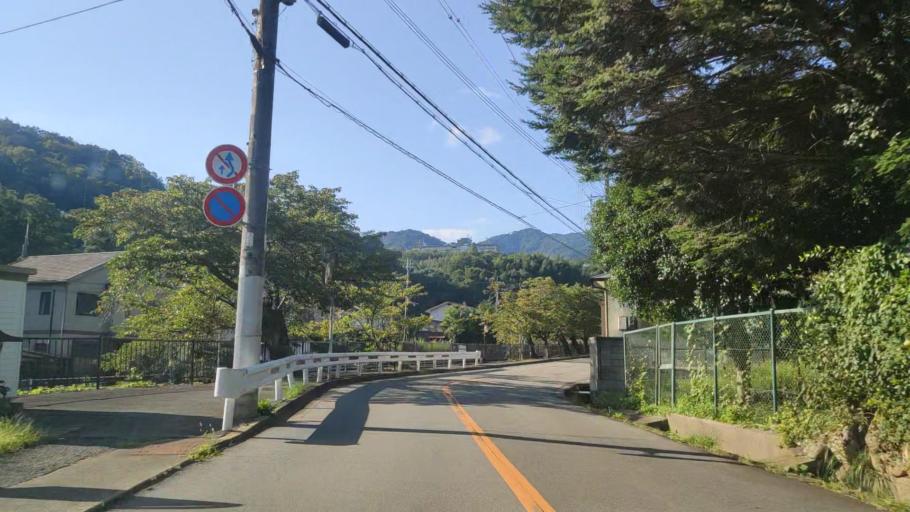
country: JP
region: Hyogo
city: Sandacho
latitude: 34.8048
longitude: 135.2496
